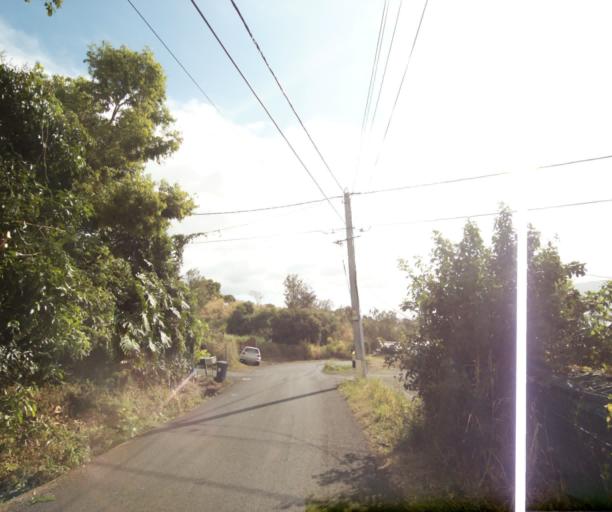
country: RE
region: Reunion
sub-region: Reunion
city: Saint-Paul
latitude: -20.9987
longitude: 55.3331
